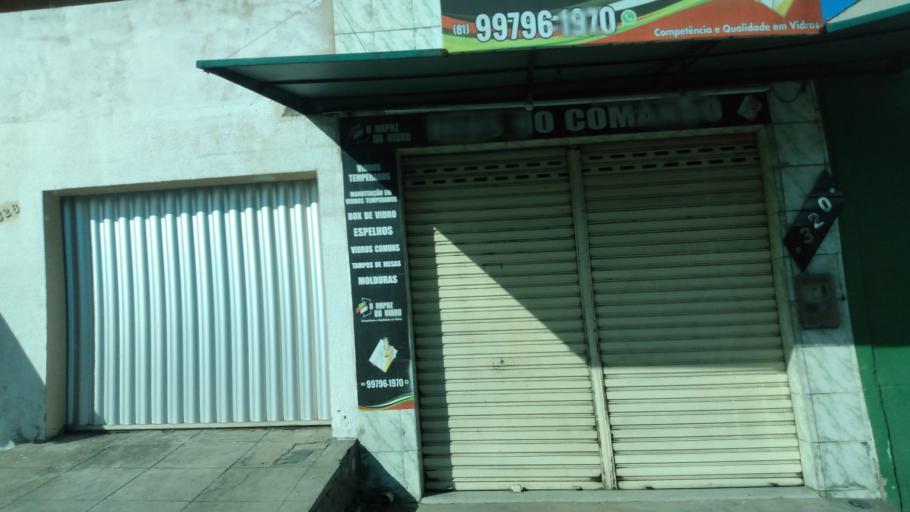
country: ET
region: Oromiya
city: Gore
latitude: 8.1989
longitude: 35.5723
